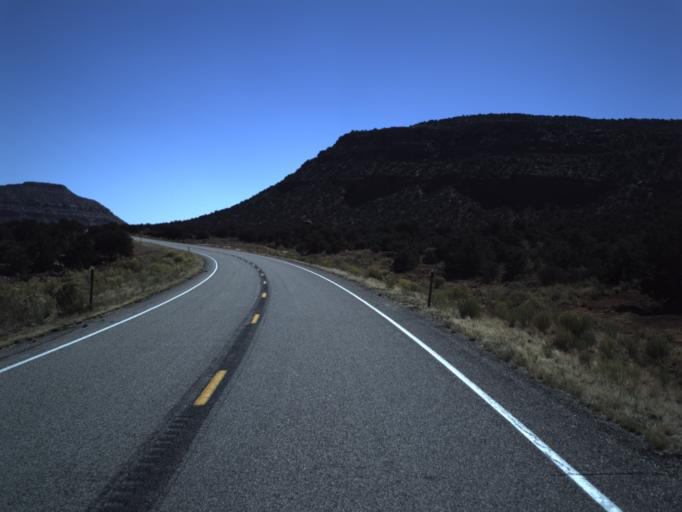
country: US
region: Utah
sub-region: San Juan County
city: Blanding
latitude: 37.6361
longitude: -110.1055
